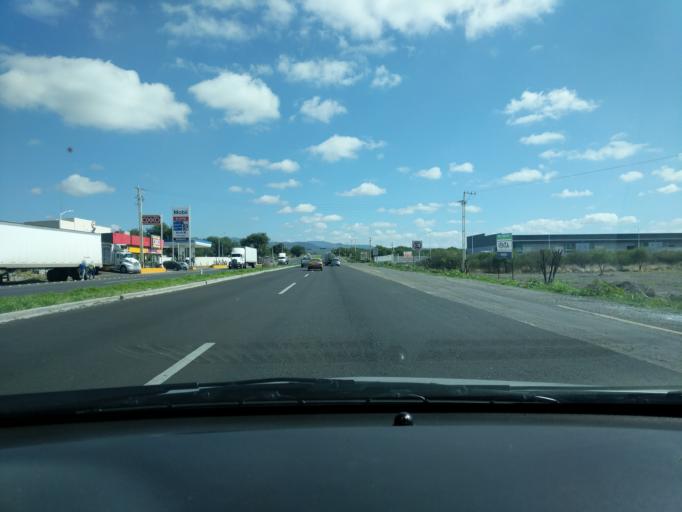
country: MX
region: Queretaro
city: Tlacote el Bajo
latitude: 20.6435
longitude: -100.5010
